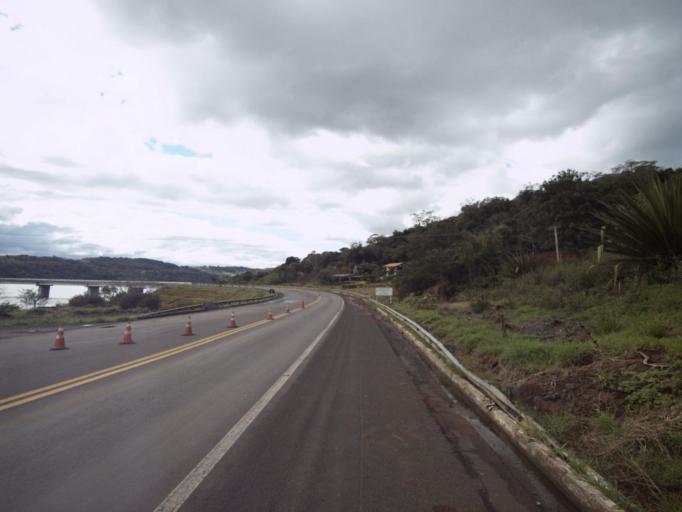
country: BR
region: Santa Catarina
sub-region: Concordia
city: Concordia
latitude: -27.3807
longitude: -51.9871
